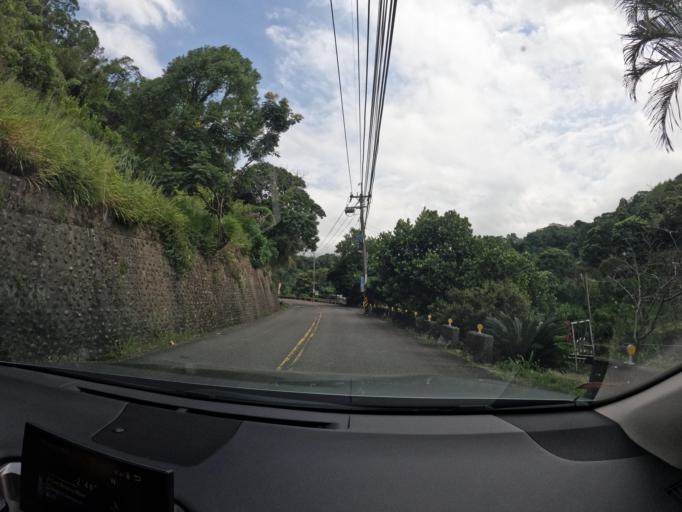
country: TW
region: Taiwan
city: Fengyuan
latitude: 24.3041
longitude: 120.8402
